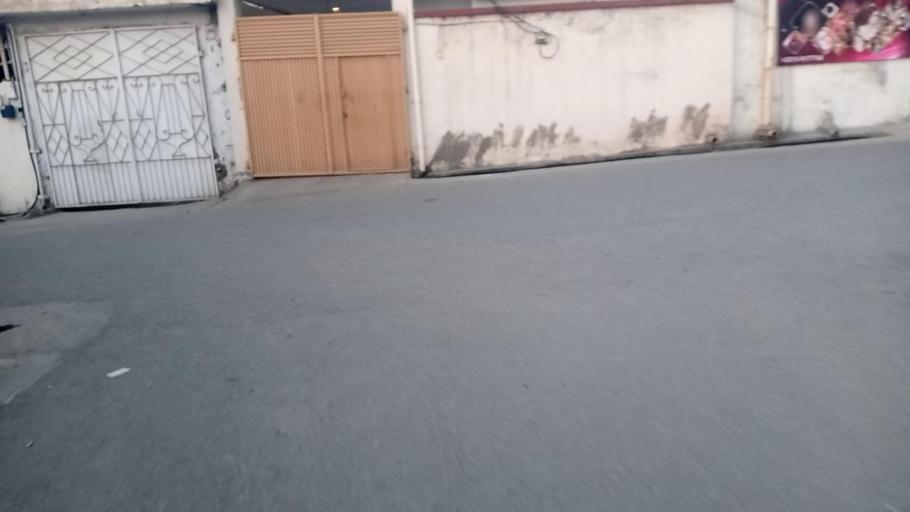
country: PK
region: Khyber Pakhtunkhwa
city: Saidu Sharif
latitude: 34.7563
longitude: 72.3613
